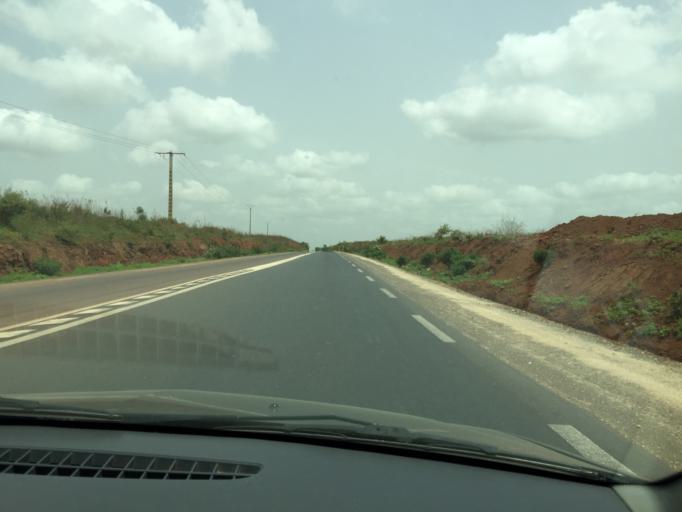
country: SN
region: Thies
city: Nguekhokh
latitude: 14.6144
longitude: -17.0522
